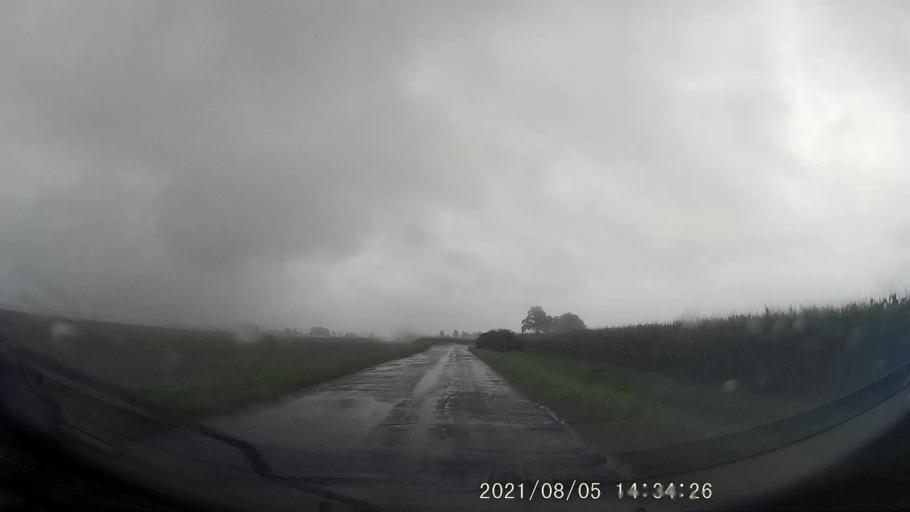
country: PL
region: Opole Voivodeship
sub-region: Powiat nyski
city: Lambinowice
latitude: 50.4679
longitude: 17.5194
